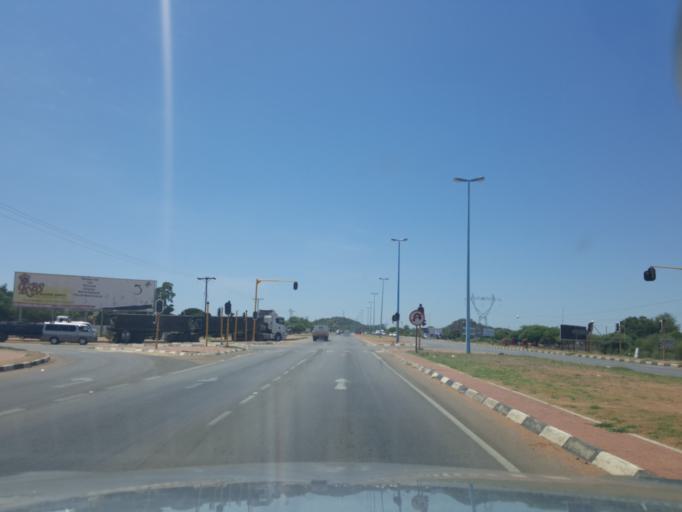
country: BW
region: Kweneng
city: Gaphatshwe
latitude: -24.5880
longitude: 25.8441
